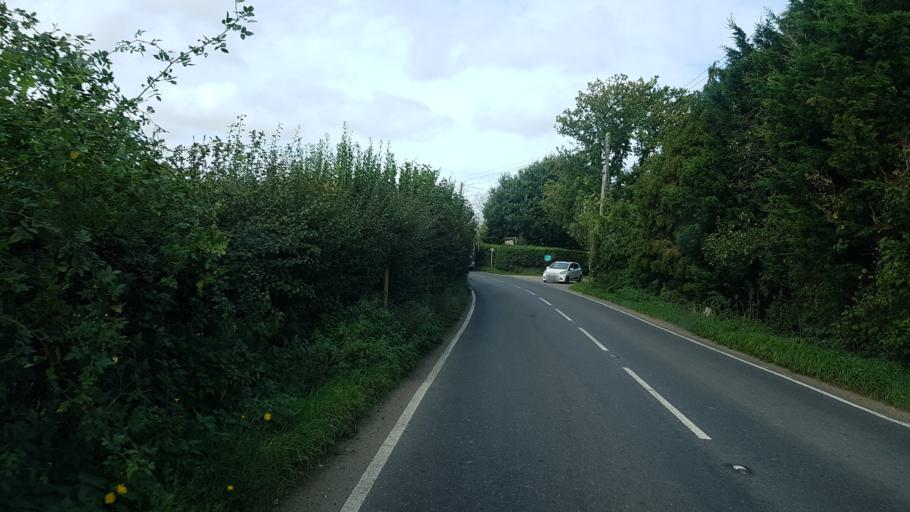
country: GB
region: England
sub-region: Kent
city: Staplehurst
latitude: 51.2251
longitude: 0.5690
